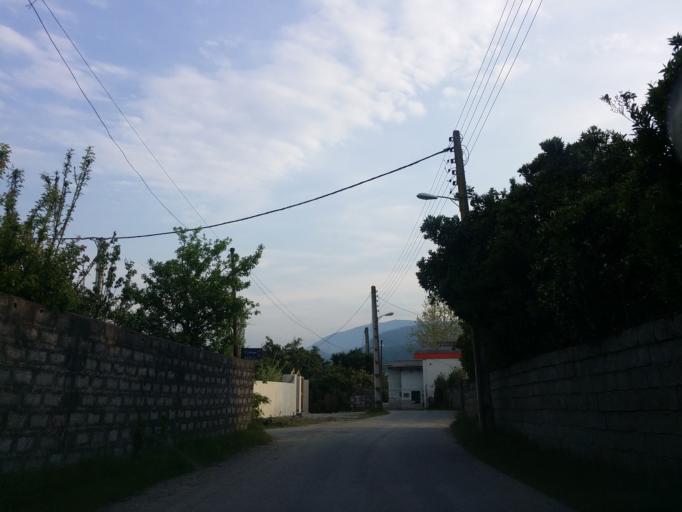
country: IR
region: Mazandaran
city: Chalus
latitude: 36.6704
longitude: 51.3704
